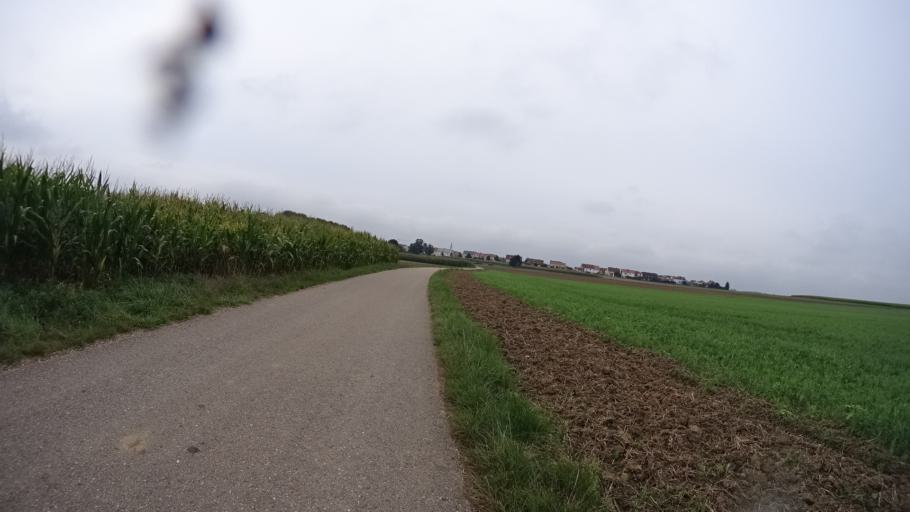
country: DE
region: Bavaria
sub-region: Upper Bavaria
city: Gaimersheim
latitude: 48.8204
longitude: 11.3644
